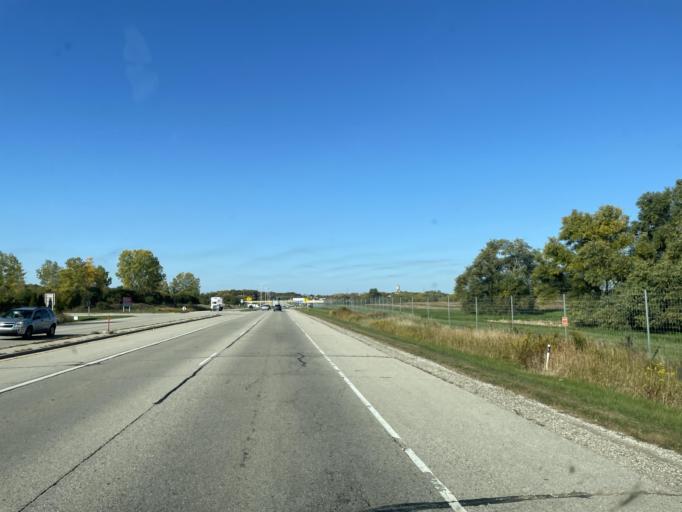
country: US
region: Wisconsin
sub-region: Kenosha County
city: Pleasant Prairie
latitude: 42.5897
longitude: -87.9442
